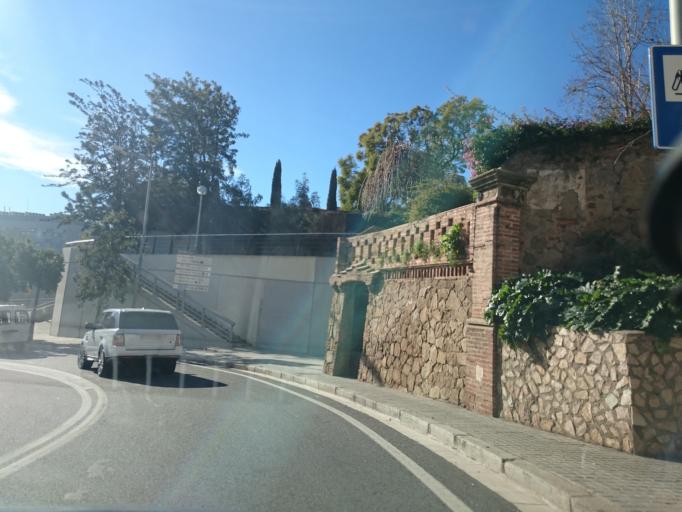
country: ES
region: Catalonia
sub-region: Provincia de Barcelona
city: Sarria-Sant Gervasi
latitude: 41.4181
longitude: 2.1384
